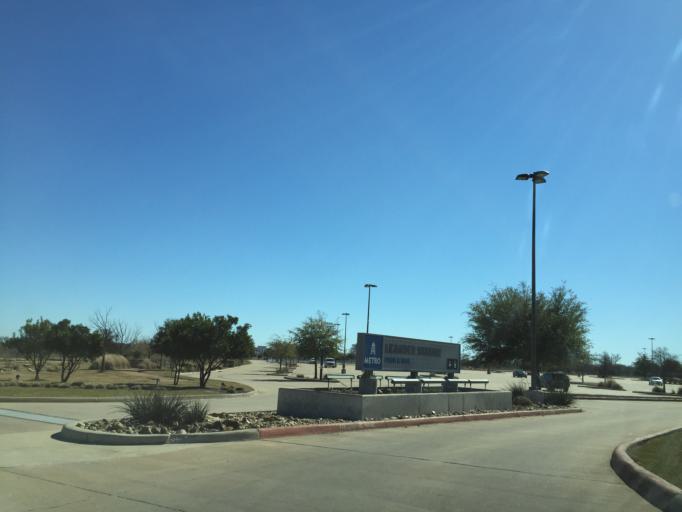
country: US
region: Texas
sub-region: Williamson County
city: Leander
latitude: 30.5880
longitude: -97.8557
